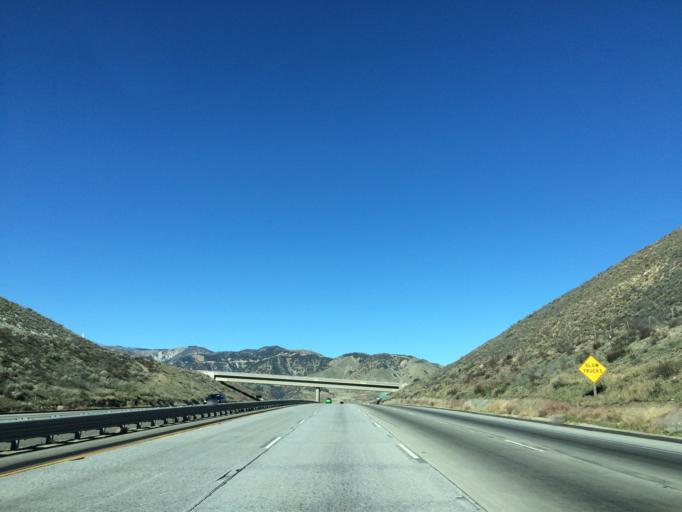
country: US
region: California
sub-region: Kern County
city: Lebec
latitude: 34.8010
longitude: -118.8739
